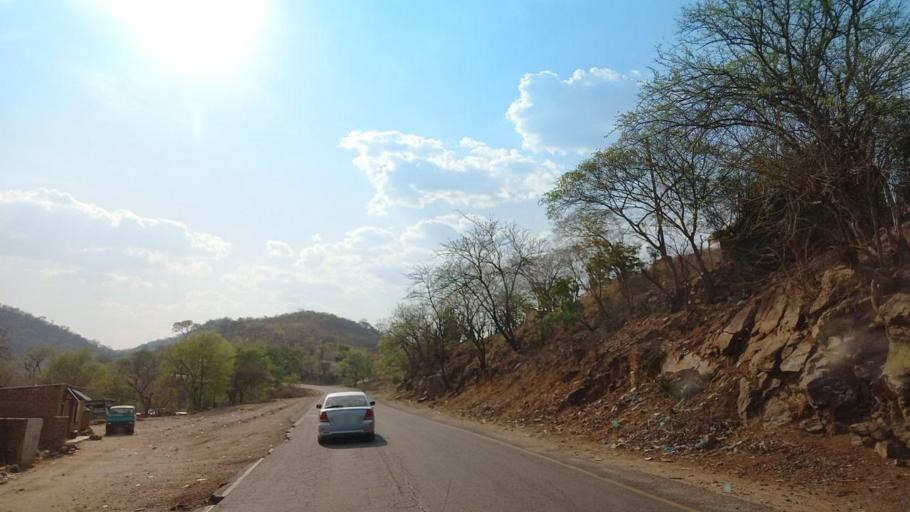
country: ZM
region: Lusaka
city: Luangwa
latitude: -14.9844
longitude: 30.2014
